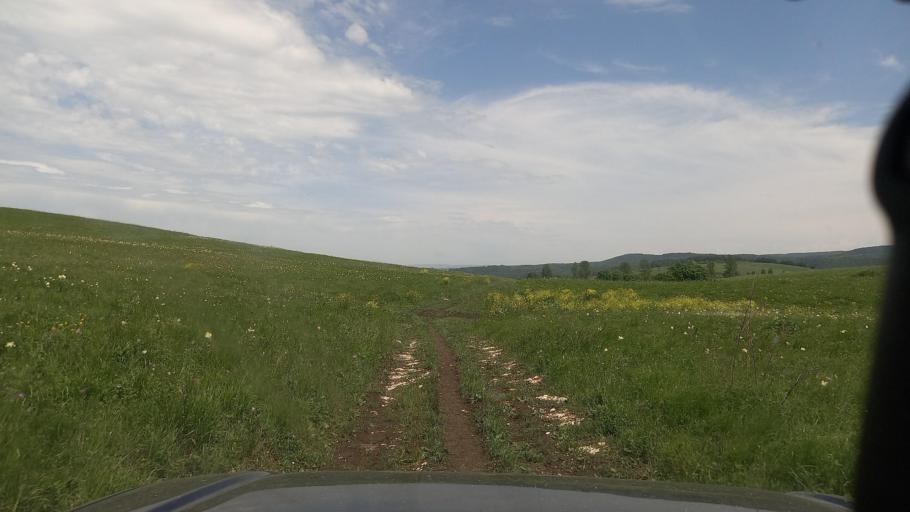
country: RU
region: Karachayevo-Cherkesiya
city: Pregradnaya
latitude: 44.0674
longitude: 41.3023
